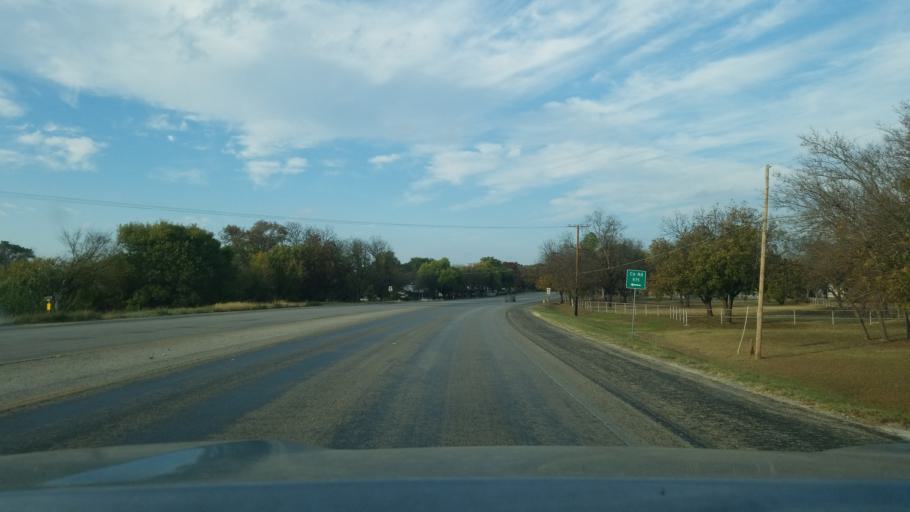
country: US
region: Texas
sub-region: Brown County
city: Early
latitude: 31.7459
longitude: -98.9644
